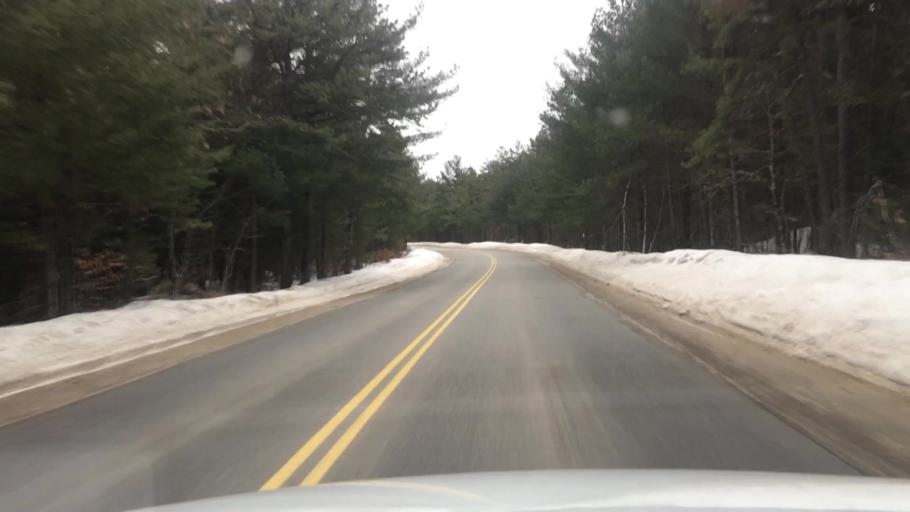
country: US
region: Maine
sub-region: York County
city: Newfield
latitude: 43.6014
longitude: -70.8781
